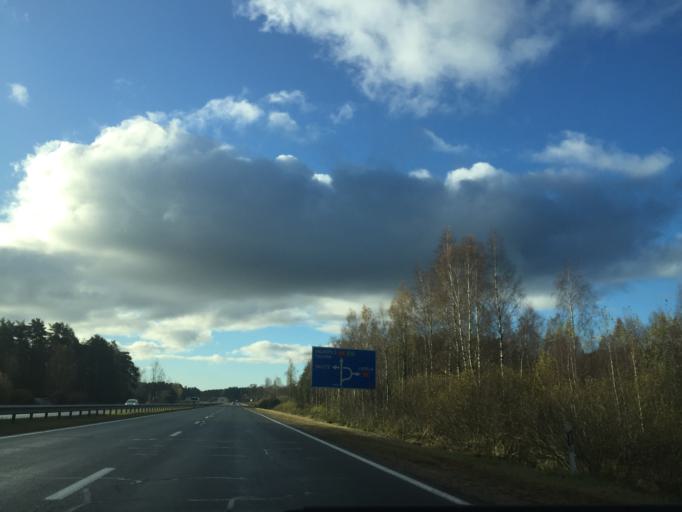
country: LV
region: Babite
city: Pinki
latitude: 56.9327
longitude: 23.9173
